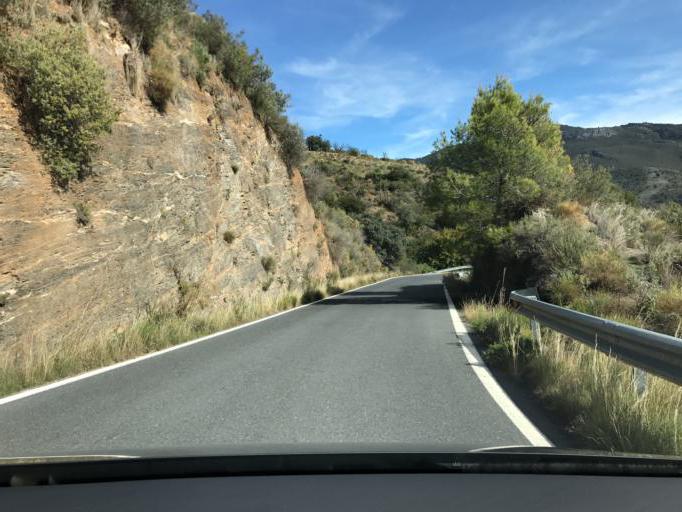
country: ES
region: Andalusia
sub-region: Provincia de Granada
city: Otivar
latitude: 36.8220
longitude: -3.6947
